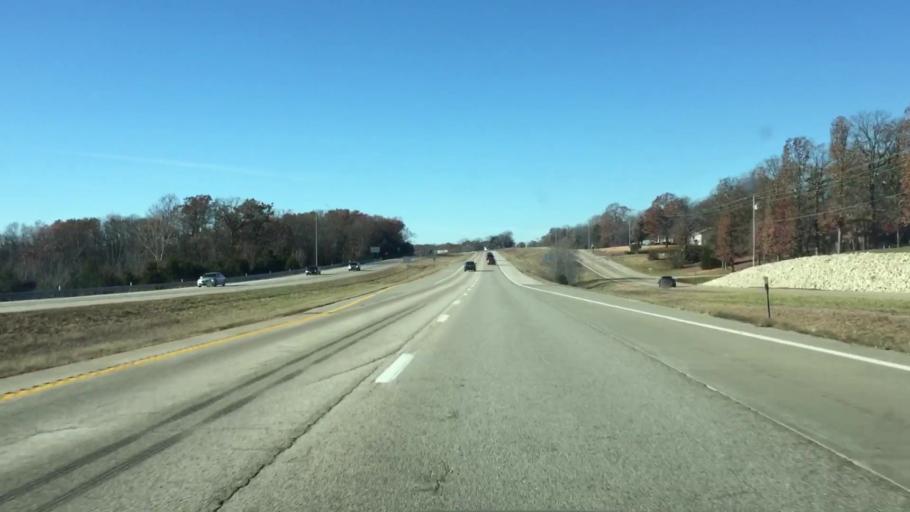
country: US
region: Missouri
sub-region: Cole County
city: Wardsville
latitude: 38.4721
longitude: -92.2827
